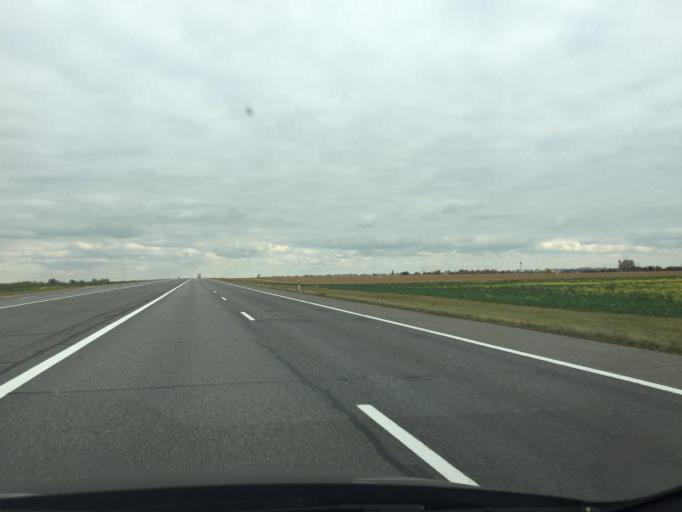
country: BY
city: Fanipol
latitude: 53.6840
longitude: 27.3076
